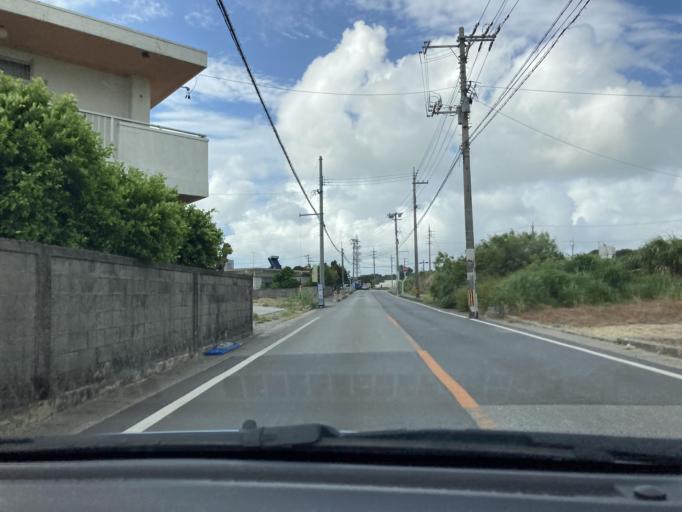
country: JP
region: Okinawa
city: Itoman
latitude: 26.1046
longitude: 127.6956
